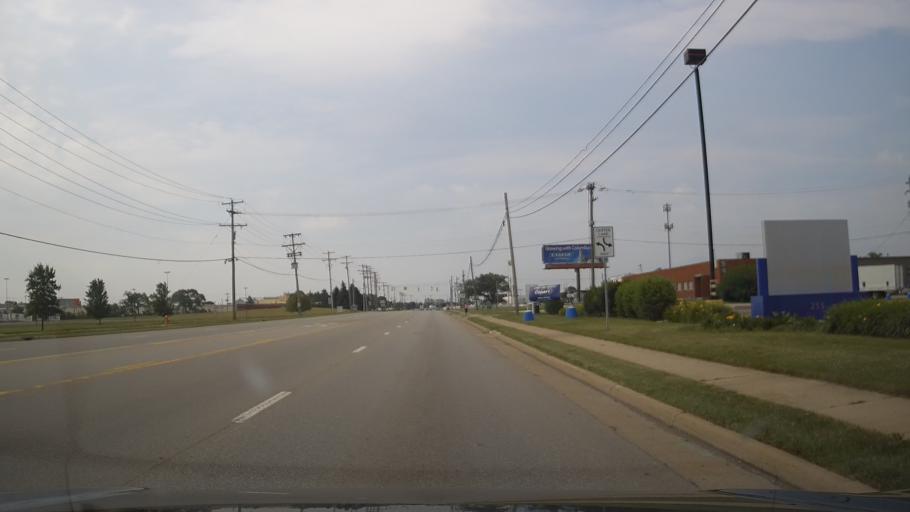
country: US
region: Ohio
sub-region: Franklin County
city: Lincoln Village
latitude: 39.9589
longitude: -83.1108
